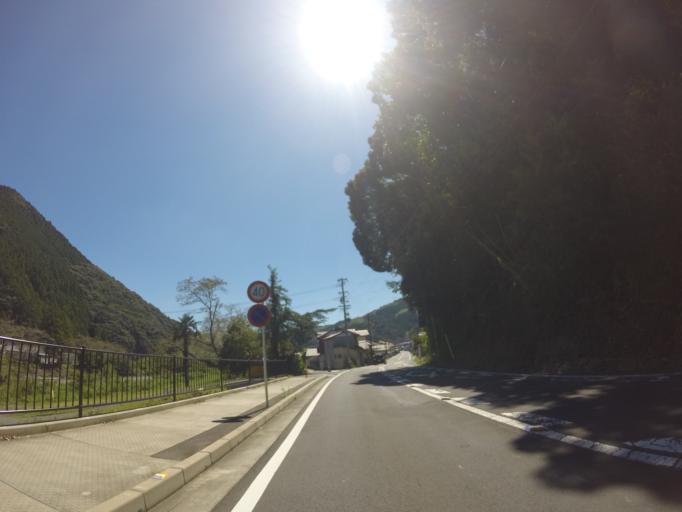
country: JP
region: Shizuoka
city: Fujieda
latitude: 34.9054
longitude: 138.1986
